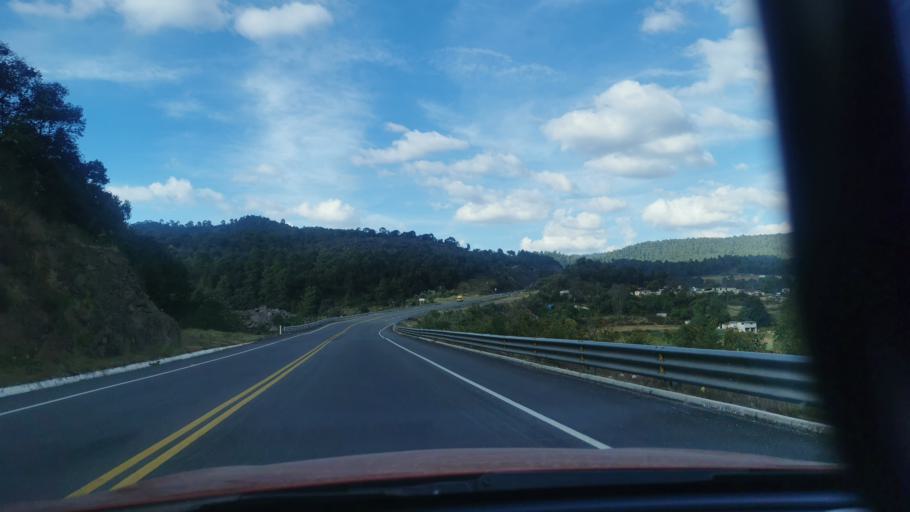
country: MX
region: Mexico
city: San Bartolo
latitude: 19.2537
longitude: -100.0679
